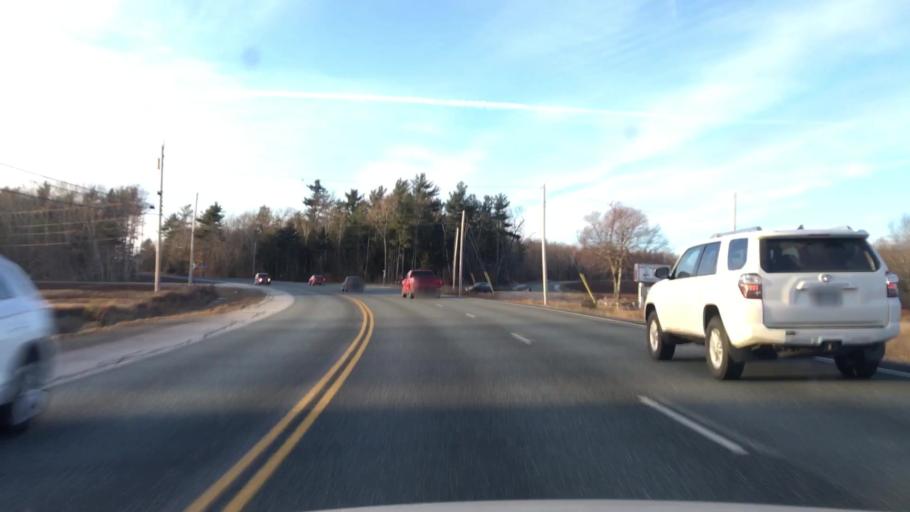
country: US
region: Maine
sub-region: Hancock County
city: Dedham
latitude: 44.6438
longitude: -68.5550
